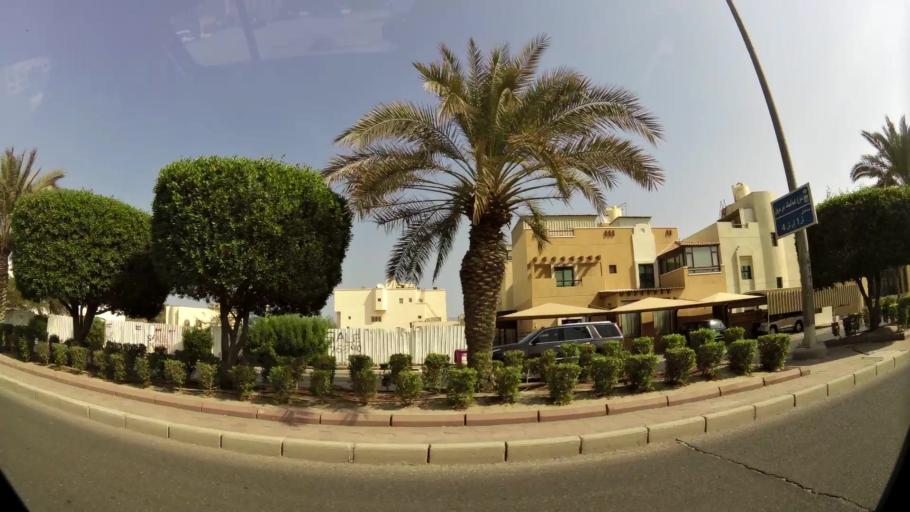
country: KW
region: Al Ahmadi
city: Al Mahbulah
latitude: 29.1366
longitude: 48.1304
